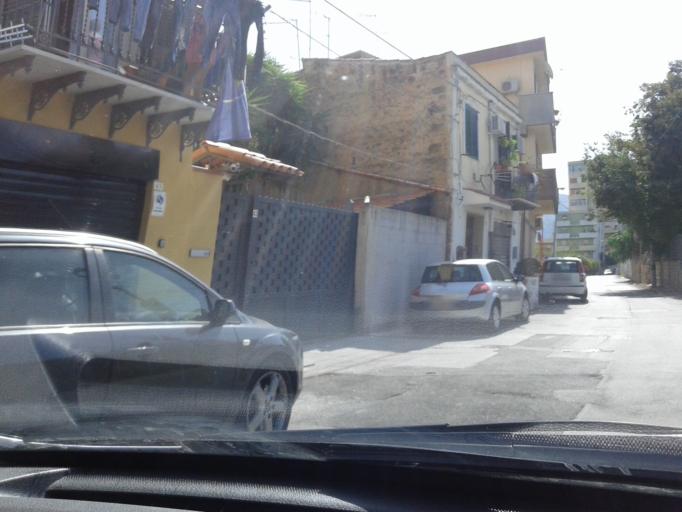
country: IT
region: Sicily
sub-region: Palermo
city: Palermo
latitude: 38.1018
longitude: 13.3211
